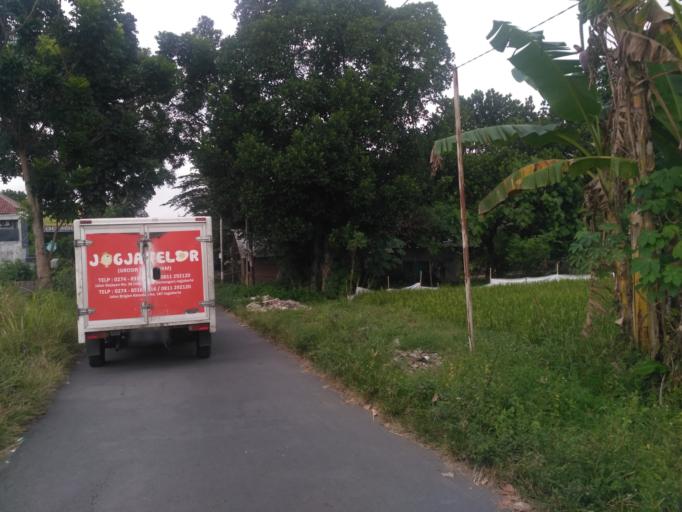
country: ID
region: Daerah Istimewa Yogyakarta
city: Melati
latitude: -7.7517
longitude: 110.3555
